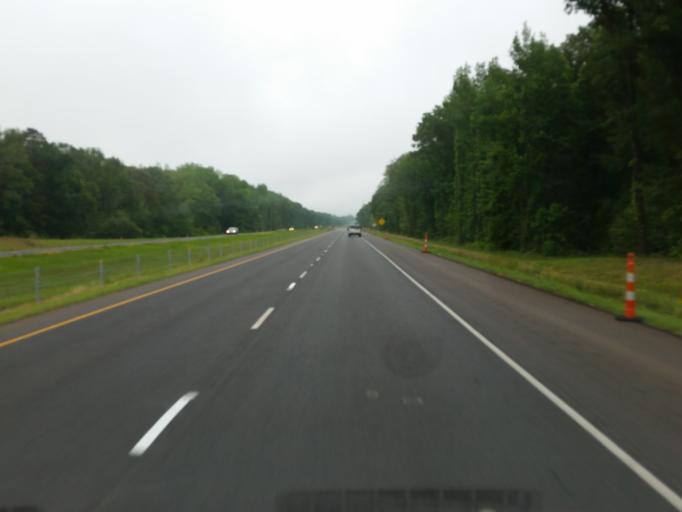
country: US
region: Louisiana
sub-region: Bienville Parish
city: Arcadia
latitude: 32.5629
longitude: -93.1016
